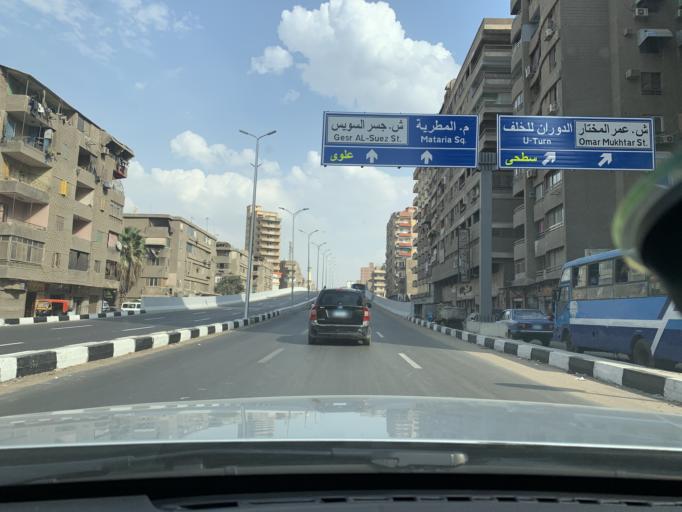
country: EG
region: Muhafazat al Qahirah
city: Cairo
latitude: 30.1277
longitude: 31.2968
